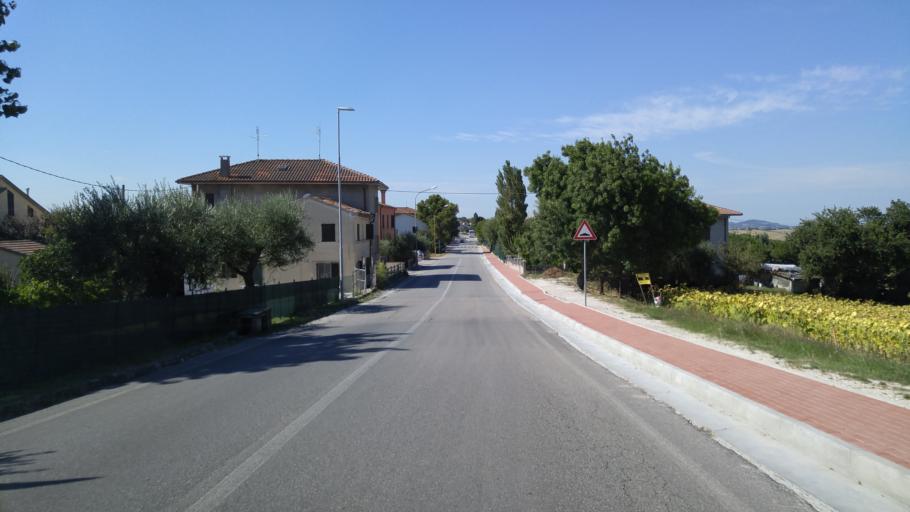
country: IT
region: The Marches
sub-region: Provincia di Pesaro e Urbino
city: San Giorgio di Pesaro
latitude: 43.7112
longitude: 12.9873
